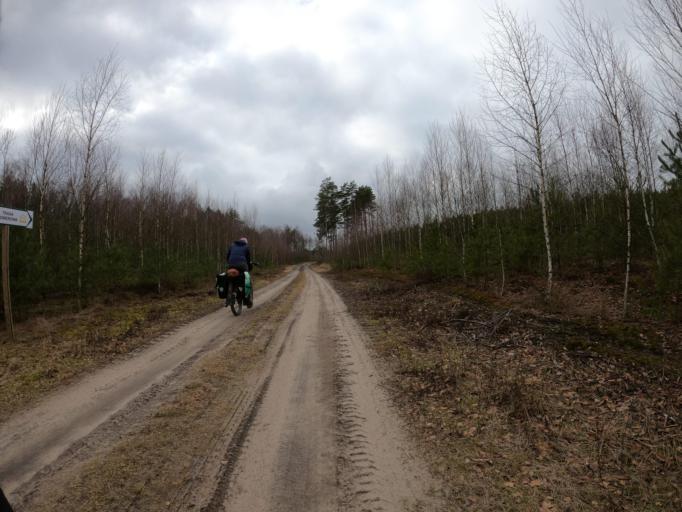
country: PL
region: Greater Poland Voivodeship
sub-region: Powiat zlotowski
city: Sypniewo
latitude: 53.4834
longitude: 16.5272
